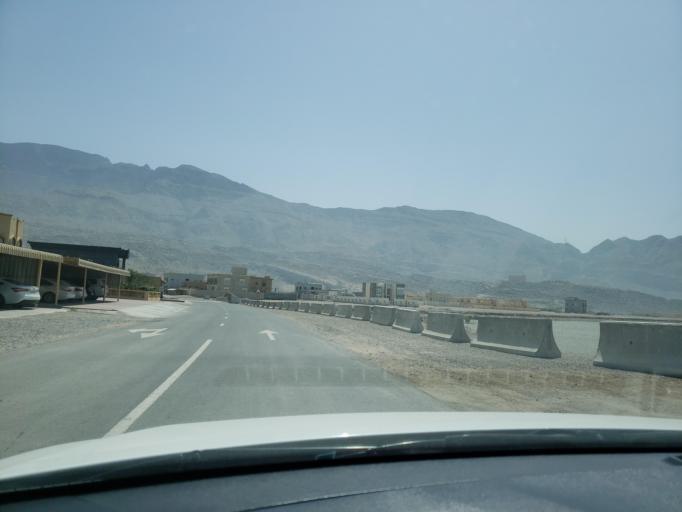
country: AE
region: Ra's al Khaymah
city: Ras al-Khaimah
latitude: 25.9166
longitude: 56.0500
